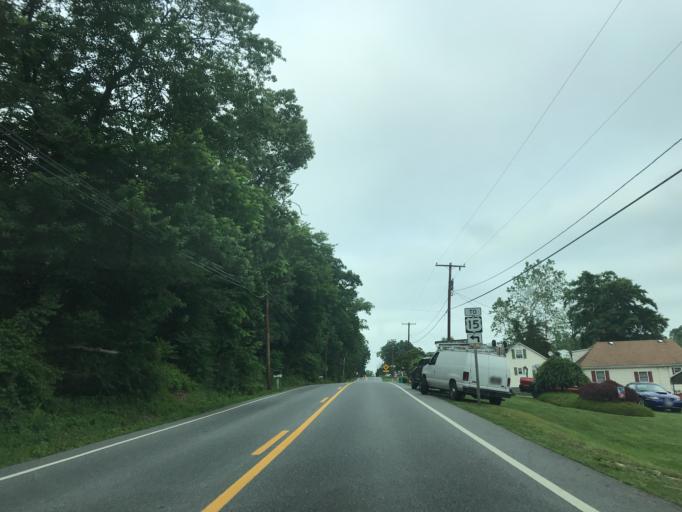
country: US
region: Maryland
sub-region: Frederick County
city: Thurmont
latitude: 39.6010
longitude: -77.4266
